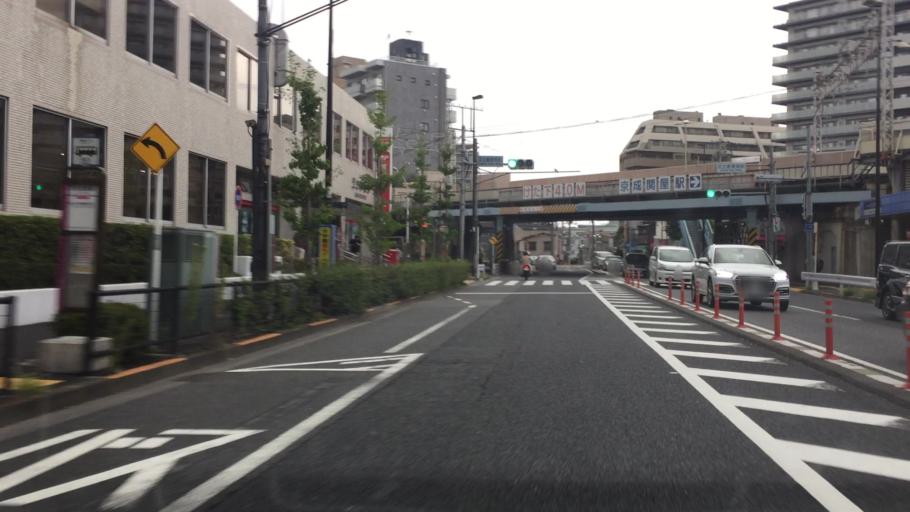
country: JP
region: Saitama
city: Soka
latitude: 35.7436
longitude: 139.8117
